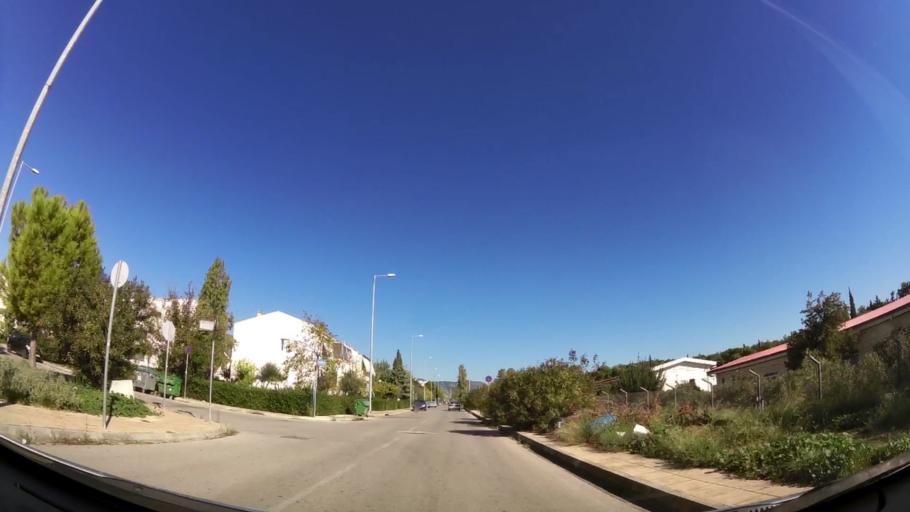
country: GR
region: Attica
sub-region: Nomarchia Anatolikis Attikis
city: Varybobi
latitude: 38.1057
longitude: 23.7713
